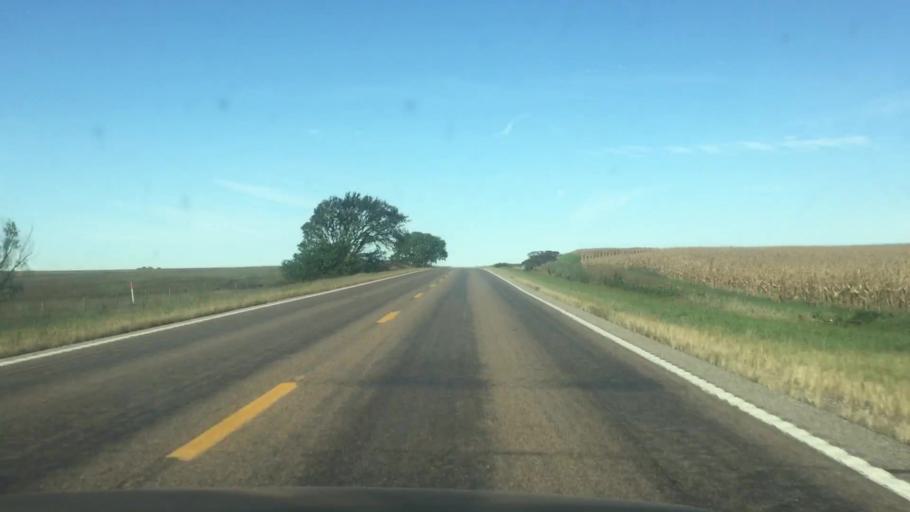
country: US
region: Nebraska
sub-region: Thayer County
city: Hebron
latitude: 40.1479
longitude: -97.4730
